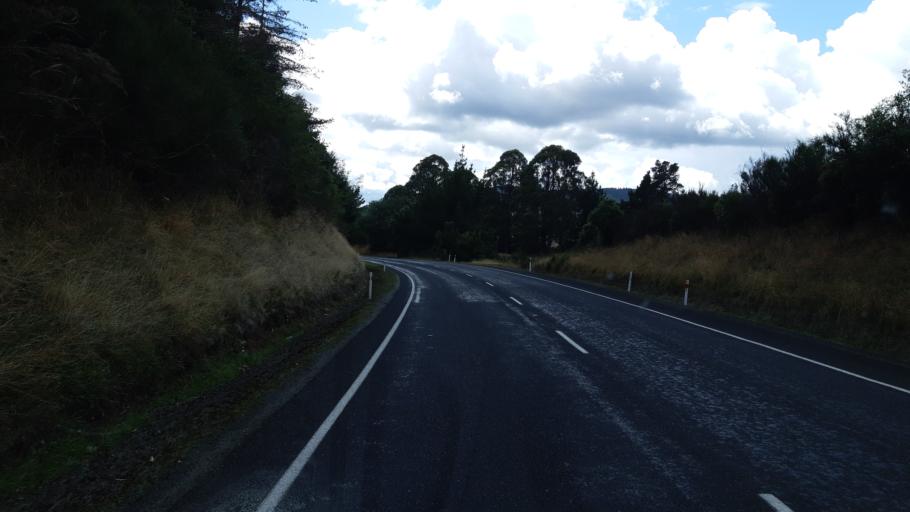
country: NZ
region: Tasman
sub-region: Tasman District
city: Wakefield
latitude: -41.5498
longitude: 172.7916
